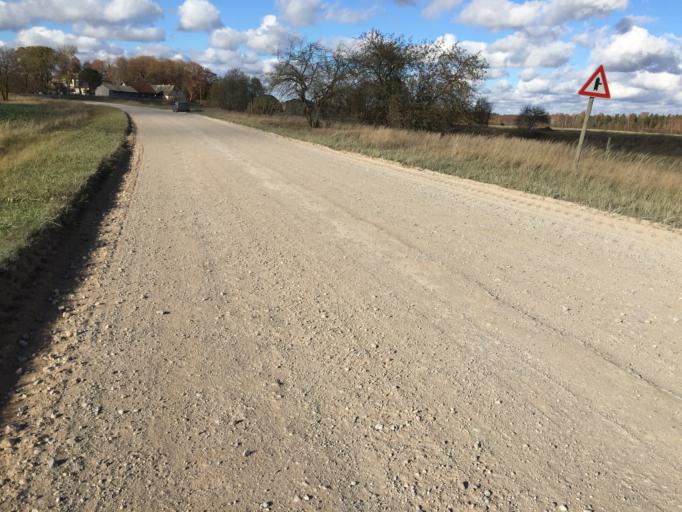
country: LV
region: Tukuma Rajons
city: Tukums
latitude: 56.9671
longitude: 22.9653
